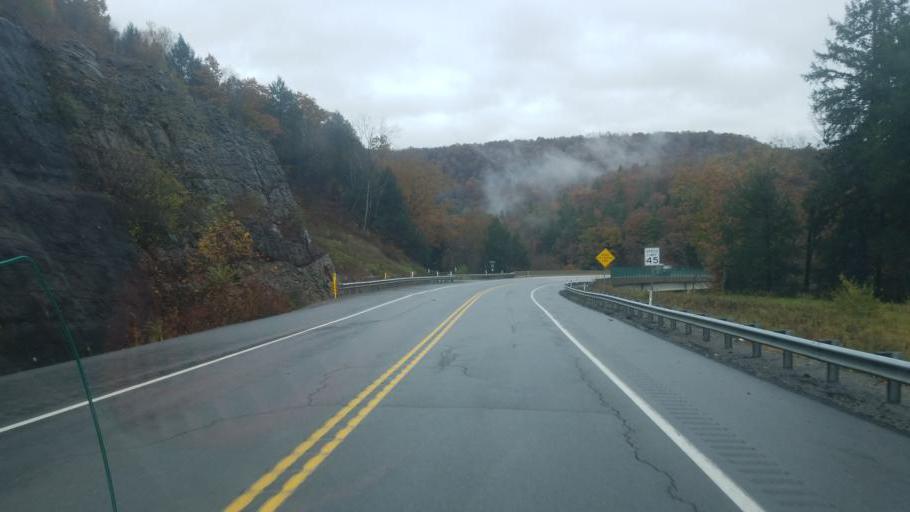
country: US
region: Pennsylvania
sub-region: Clearfield County
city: Clearfield
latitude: 41.0464
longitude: -78.3827
